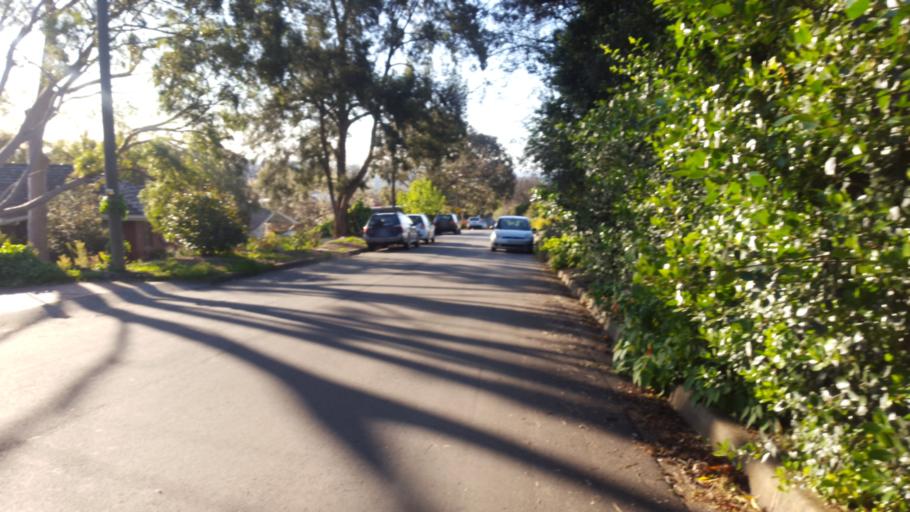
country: AU
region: South Australia
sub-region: Burnside
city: Beaumont
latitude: -34.9549
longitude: 138.6575
